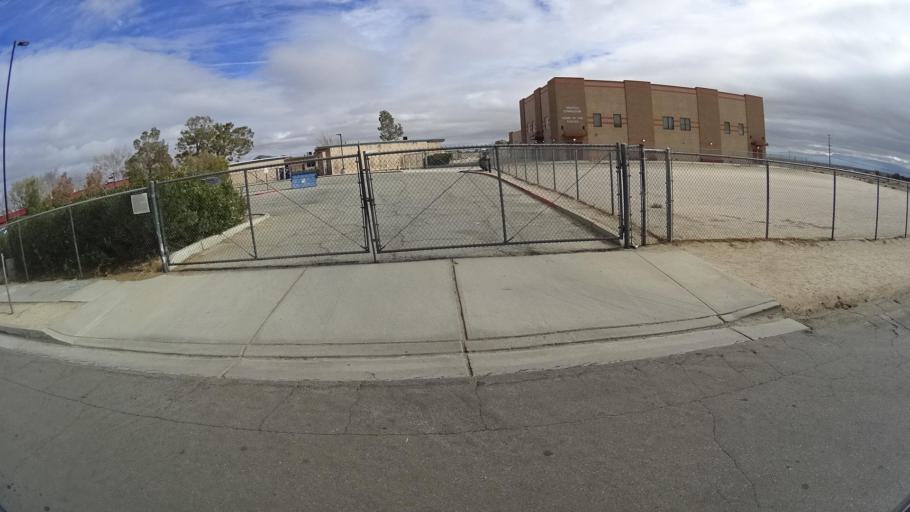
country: US
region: California
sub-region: Kern County
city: Rosamond
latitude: 34.8652
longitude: -118.2291
